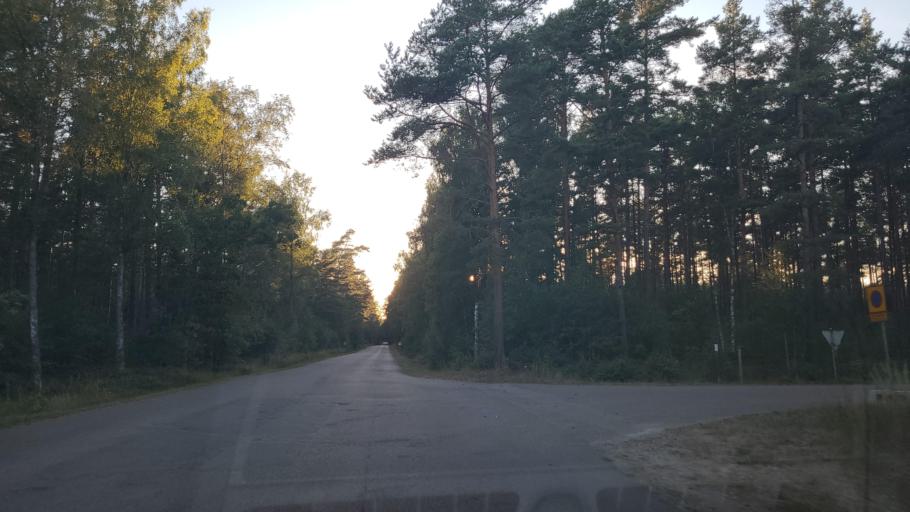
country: SE
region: Kalmar
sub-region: Borgholms Kommun
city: Borgholm
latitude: 57.2757
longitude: 17.0415
